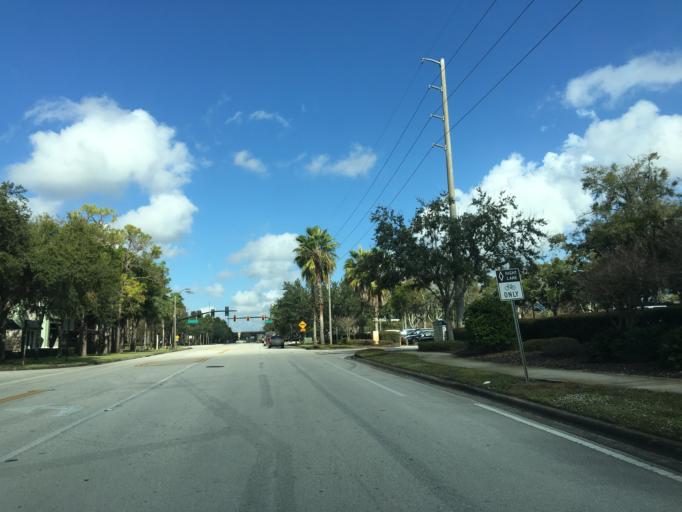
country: US
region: Florida
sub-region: Orange County
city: Eatonville
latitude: 28.6263
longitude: -81.3984
